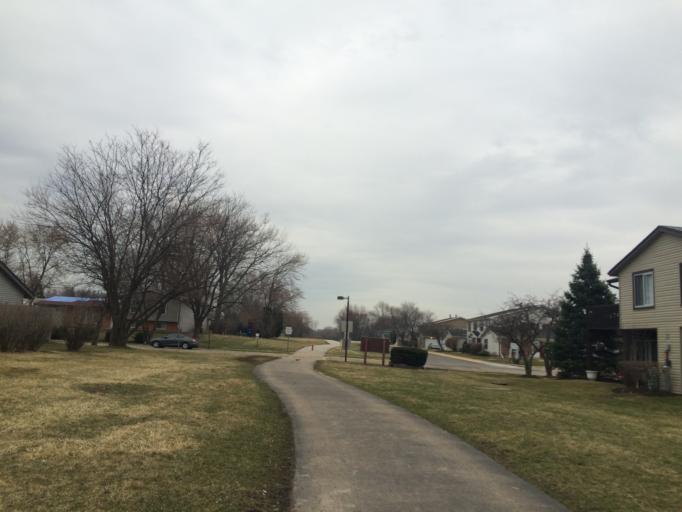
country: US
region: Illinois
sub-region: DuPage County
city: Hanover Park
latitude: 42.0103
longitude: -88.1419
